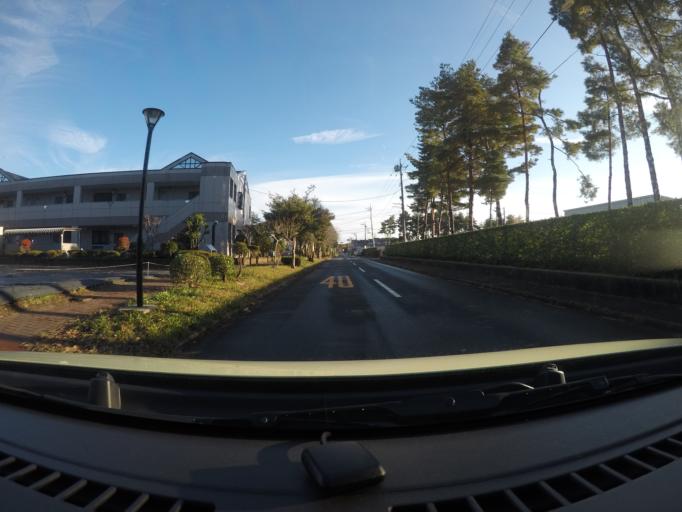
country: JP
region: Ibaraki
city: Tsukuba
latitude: 36.1292
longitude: 140.0876
